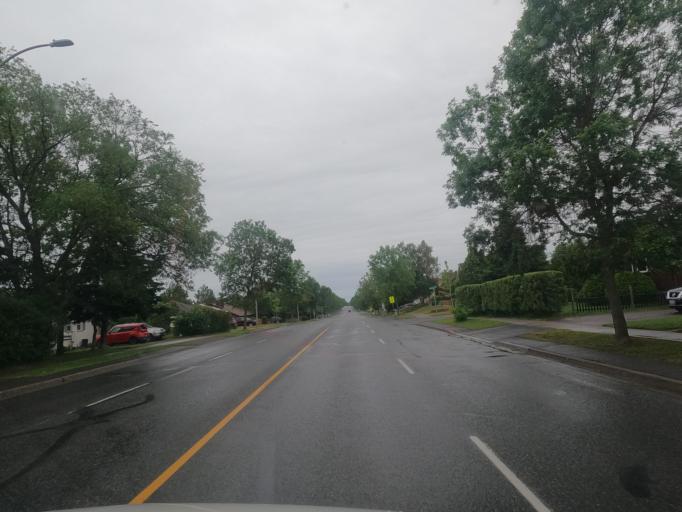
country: CA
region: Ontario
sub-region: Thunder Bay District
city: Thunder Bay
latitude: 48.4665
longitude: -89.1823
